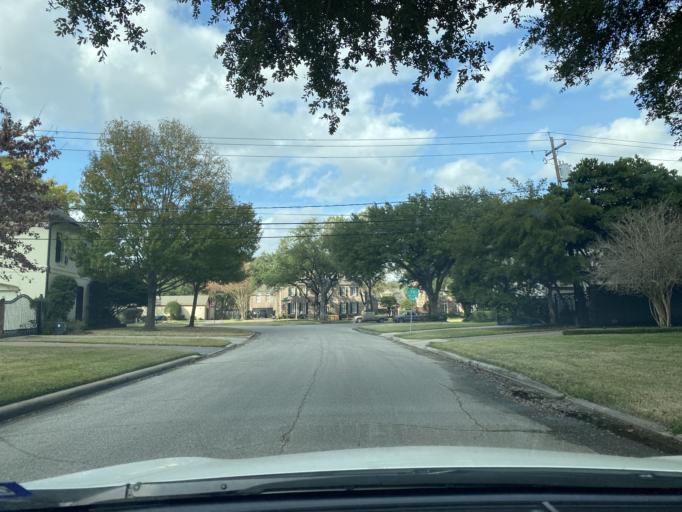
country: US
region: Texas
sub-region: Harris County
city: Hunters Creek Village
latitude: 29.7513
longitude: -95.4710
